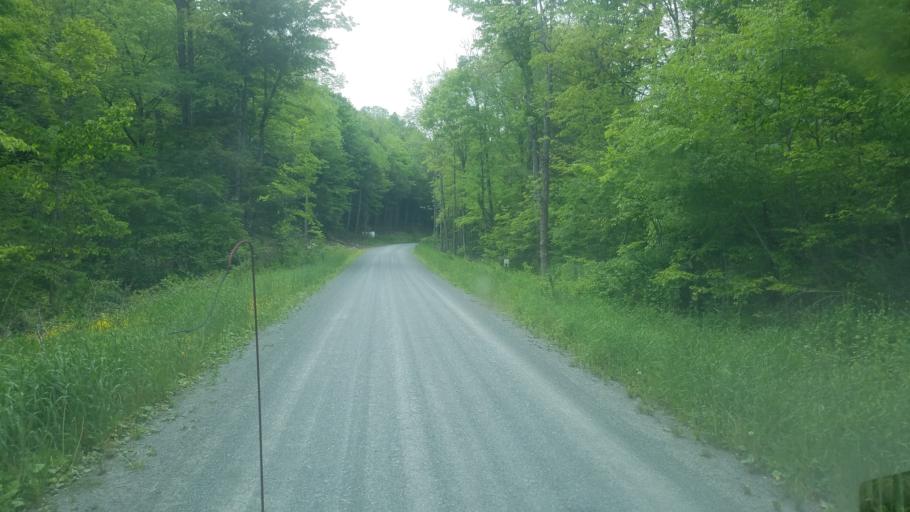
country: US
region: Pennsylvania
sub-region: Tioga County
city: Westfield
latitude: 41.8366
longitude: -77.5970
